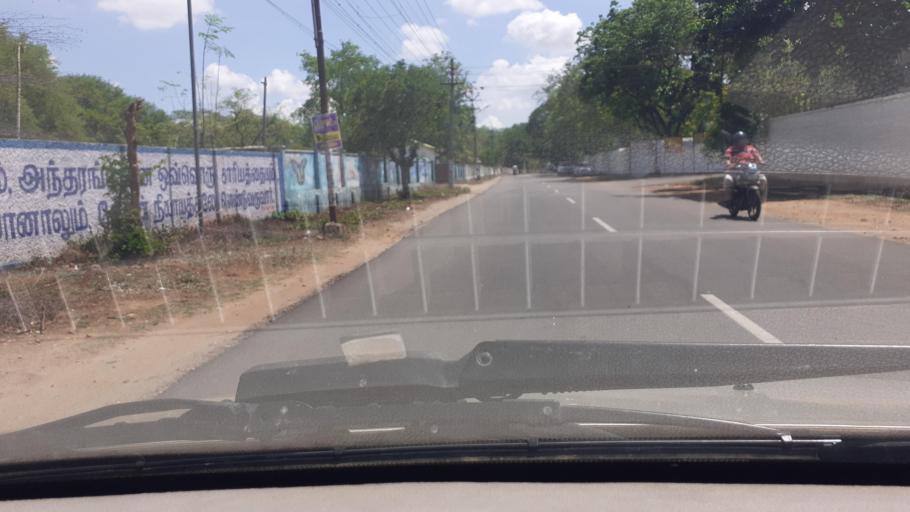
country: IN
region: Tamil Nadu
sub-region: Tirunelveli Kattabo
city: Tirunelveli
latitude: 8.7183
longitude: 77.7454
